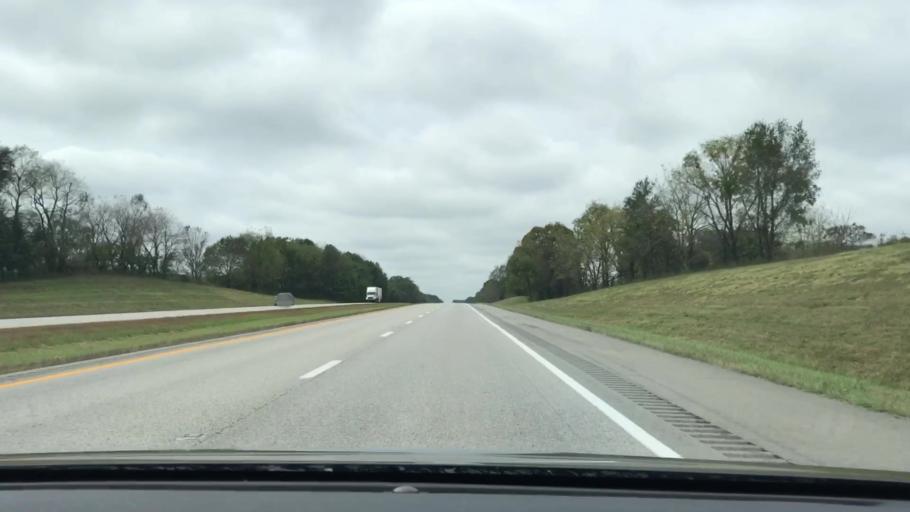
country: US
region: Kentucky
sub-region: Russell County
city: Russell Springs
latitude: 37.0730
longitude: -84.9714
